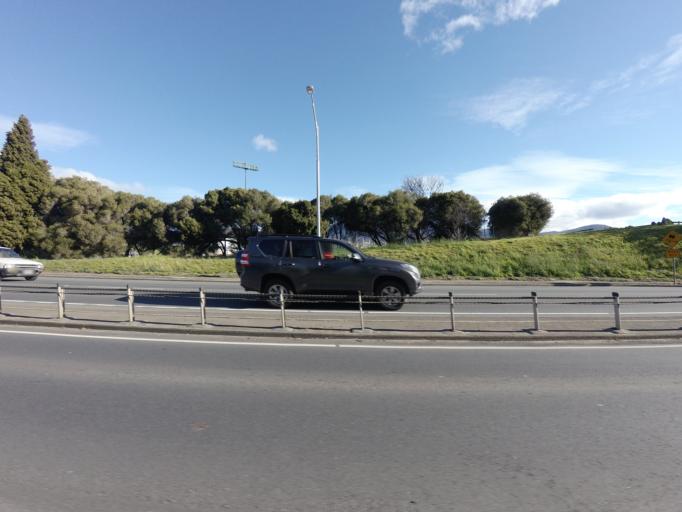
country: AU
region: Tasmania
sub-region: Hobart
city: New Town
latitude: -42.8521
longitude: 147.3155
